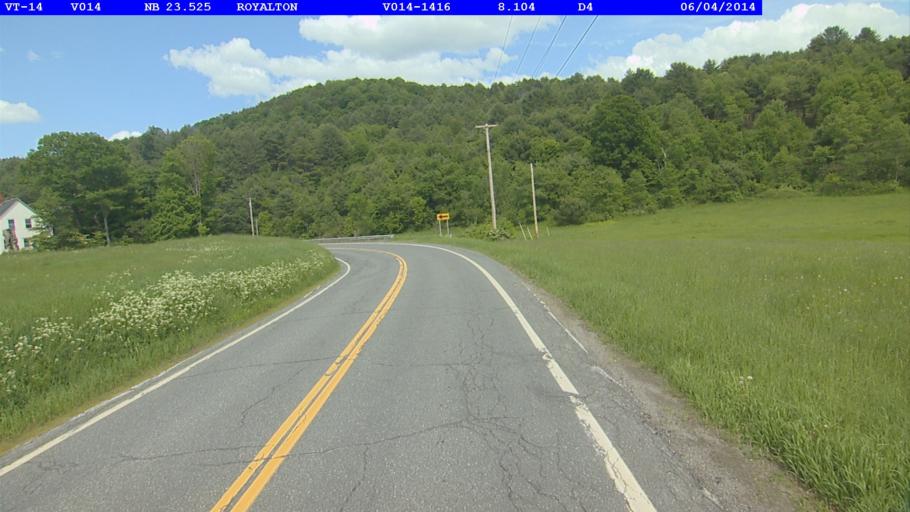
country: US
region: Vermont
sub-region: Orange County
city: Randolph
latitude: 43.8498
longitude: -72.5842
